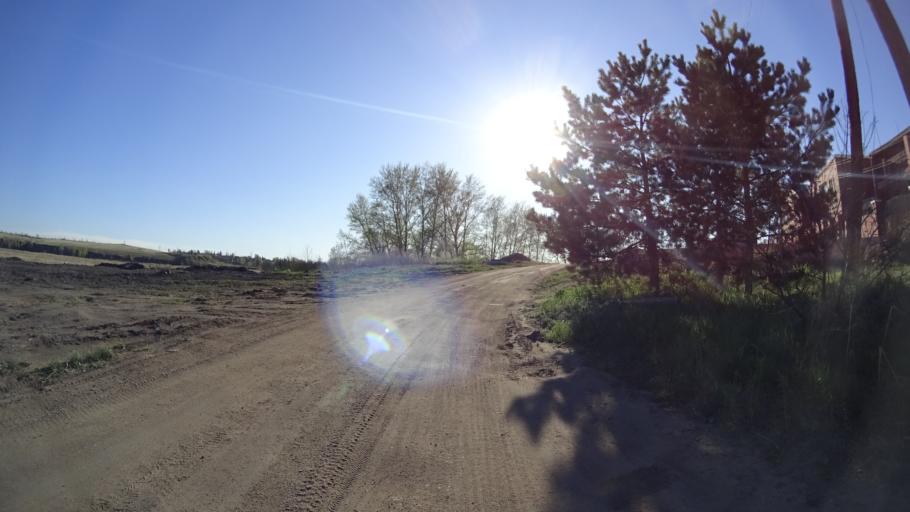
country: RU
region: Chelyabinsk
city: Troitsk
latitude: 54.0683
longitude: 61.5358
